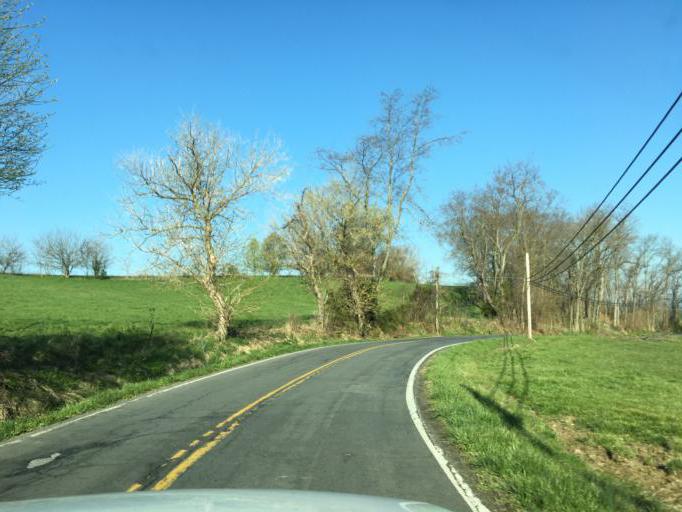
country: US
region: Maryland
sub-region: Frederick County
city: Walkersville
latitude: 39.4913
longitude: -77.3161
